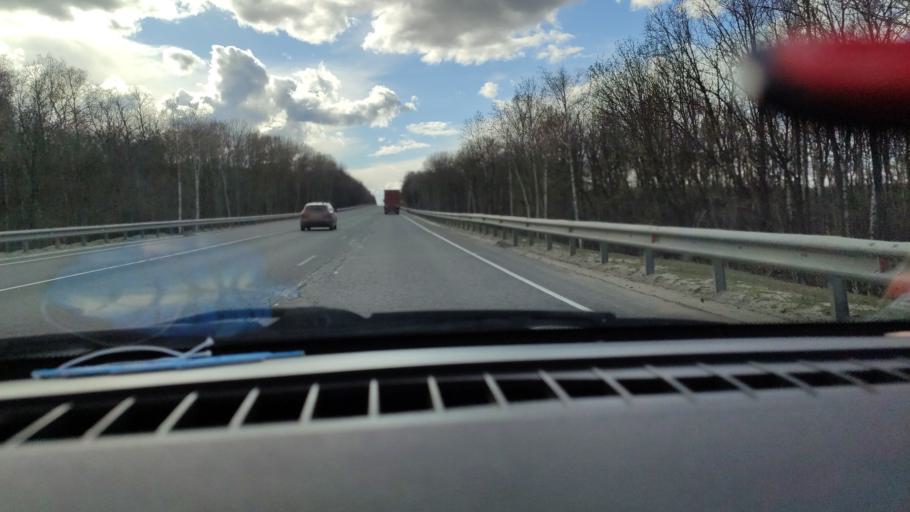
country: RU
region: Saratov
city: Vol'sk
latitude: 52.1075
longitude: 47.4115
